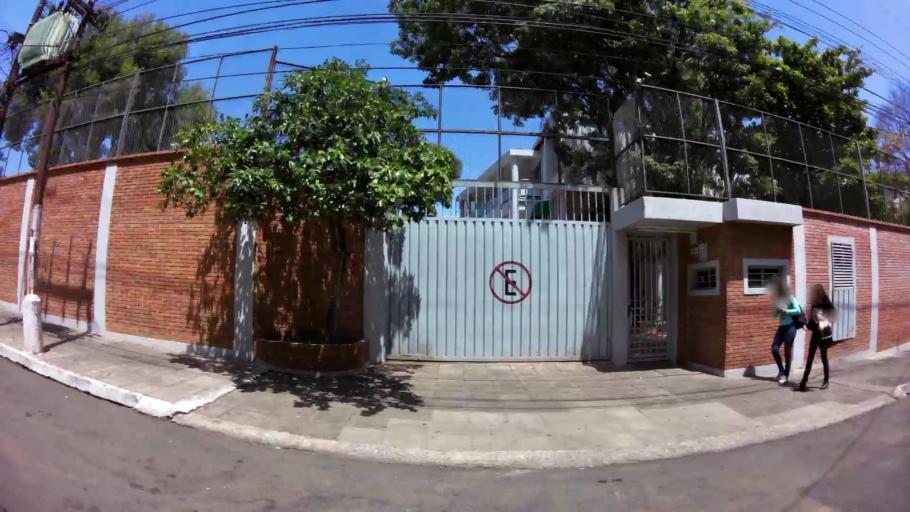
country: PY
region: Central
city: San Lorenzo
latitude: -25.3437
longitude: -57.5096
